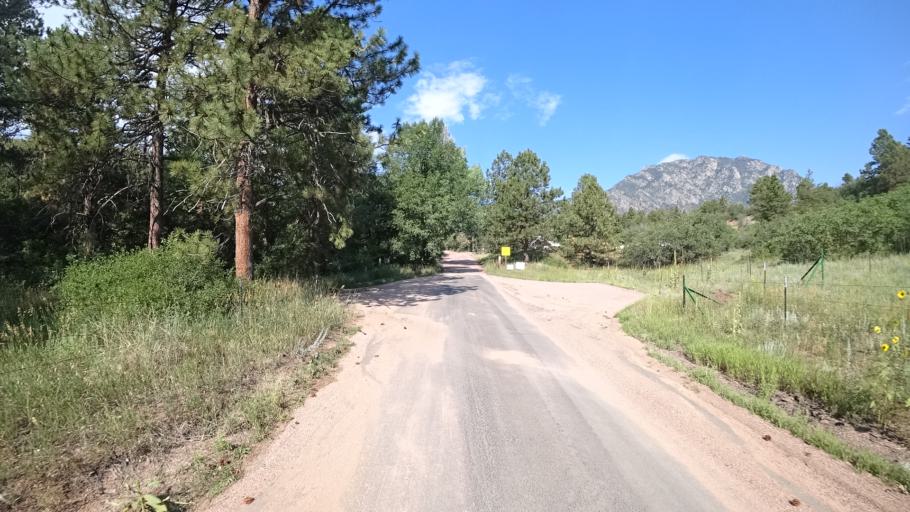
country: US
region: Colorado
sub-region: El Paso County
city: Fort Carson
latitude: 38.7191
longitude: -104.8302
